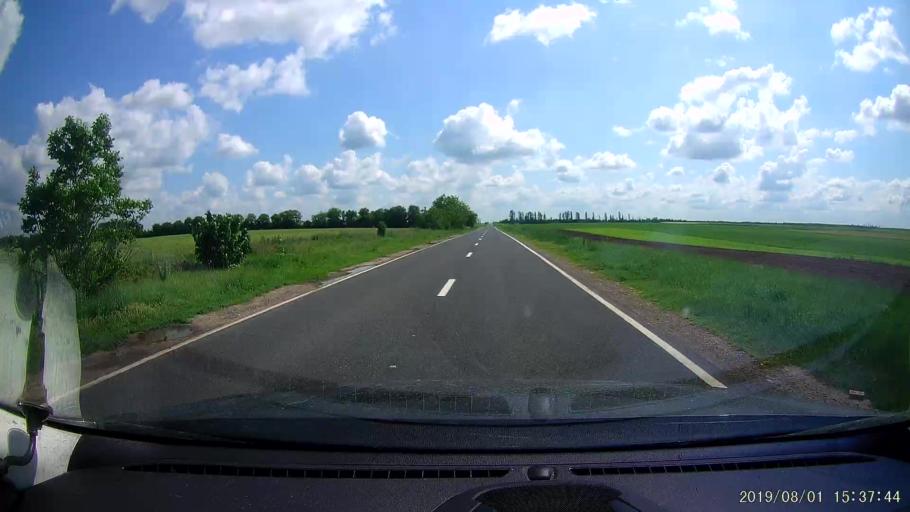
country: RO
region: Braila
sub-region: Comuna Insuratei
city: Insuratei
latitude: 44.8977
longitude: 27.5859
